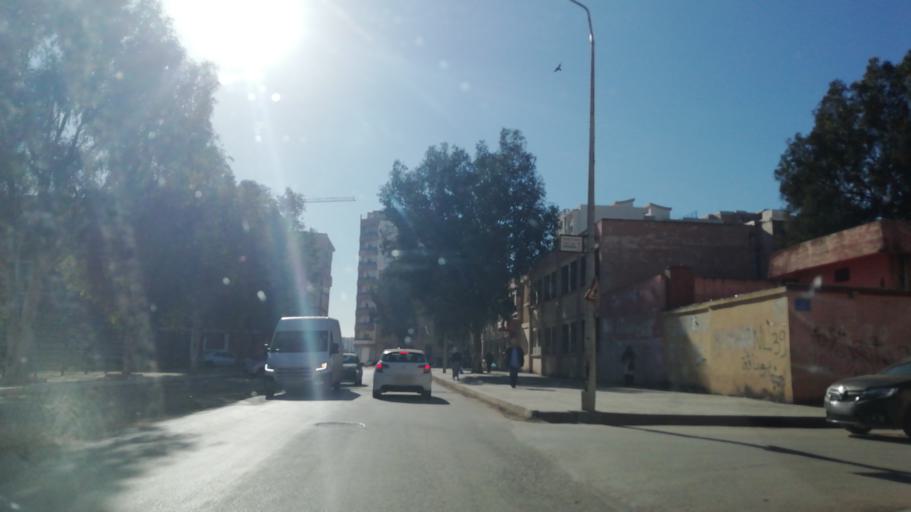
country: DZ
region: Oran
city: Oran
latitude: 35.6682
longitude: -0.6489
